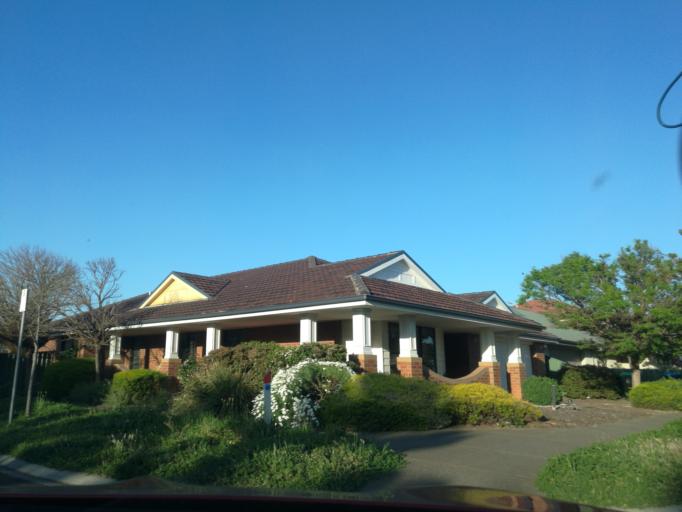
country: AU
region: Victoria
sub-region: Wyndham
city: Williams Landing
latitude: -37.8860
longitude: 144.7434
